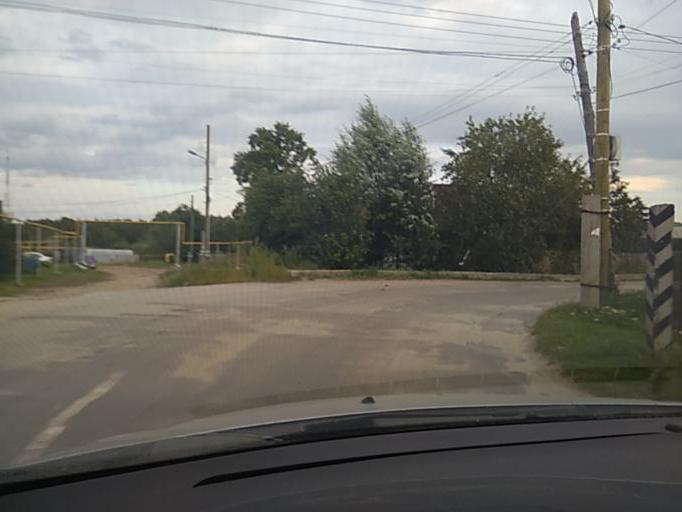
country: RU
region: Chelyabinsk
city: Kyshtym
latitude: 55.6972
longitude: 60.5323
